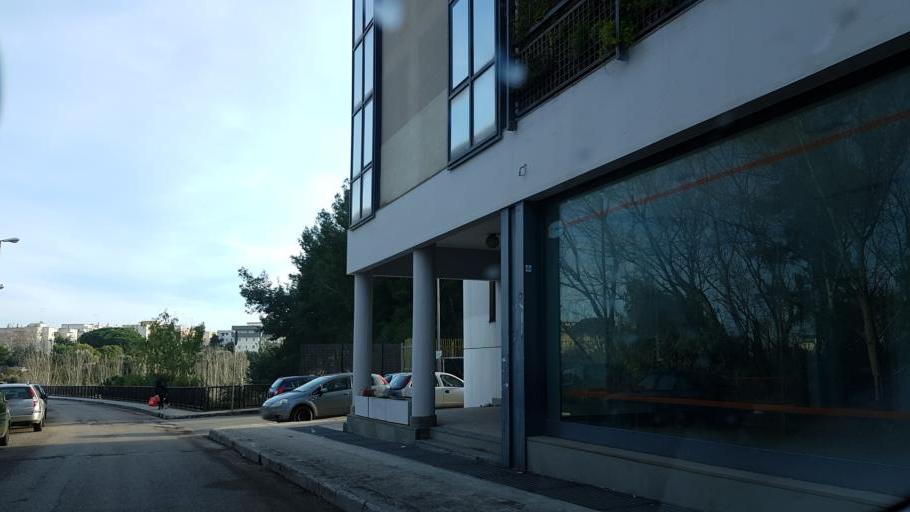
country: IT
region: Apulia
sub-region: Provincia di Brindisi
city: Brindisi
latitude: 40.6301
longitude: 17.9385
